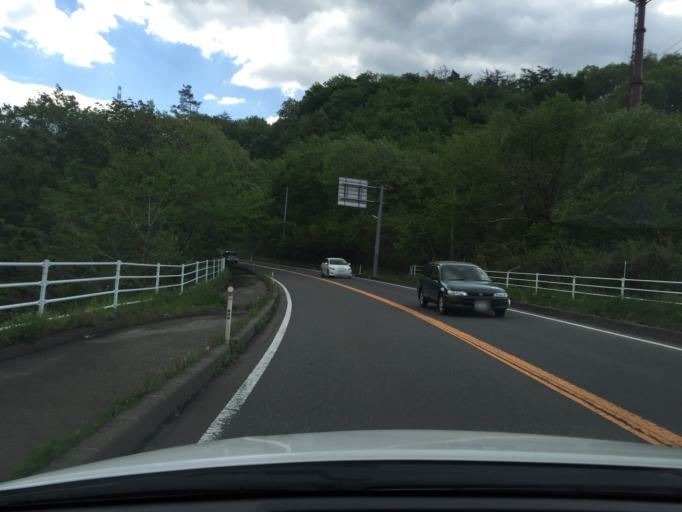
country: JP
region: Fukushima
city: Fukushima-shi
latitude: 37.6998
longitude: 140.5092
